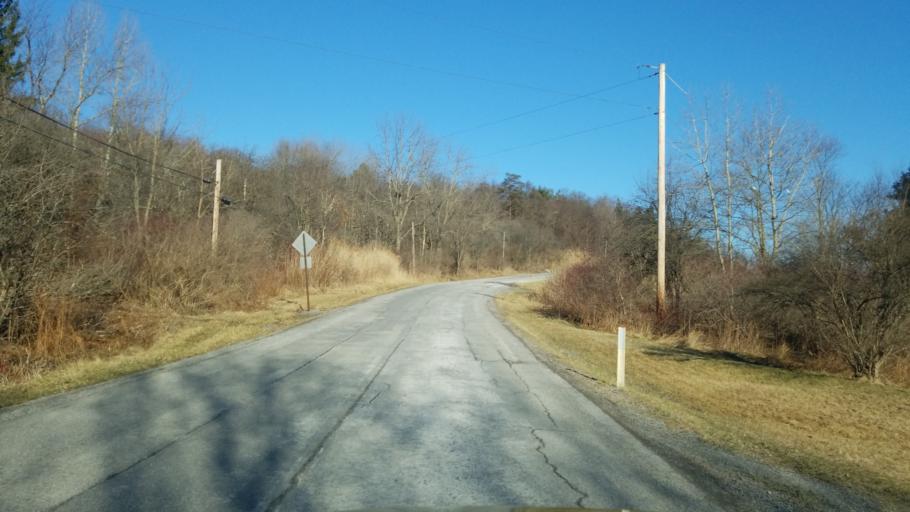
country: US
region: Pennsylvania
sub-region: Jefferson County
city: Sykesville
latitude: 41.0472
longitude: -78.7723
